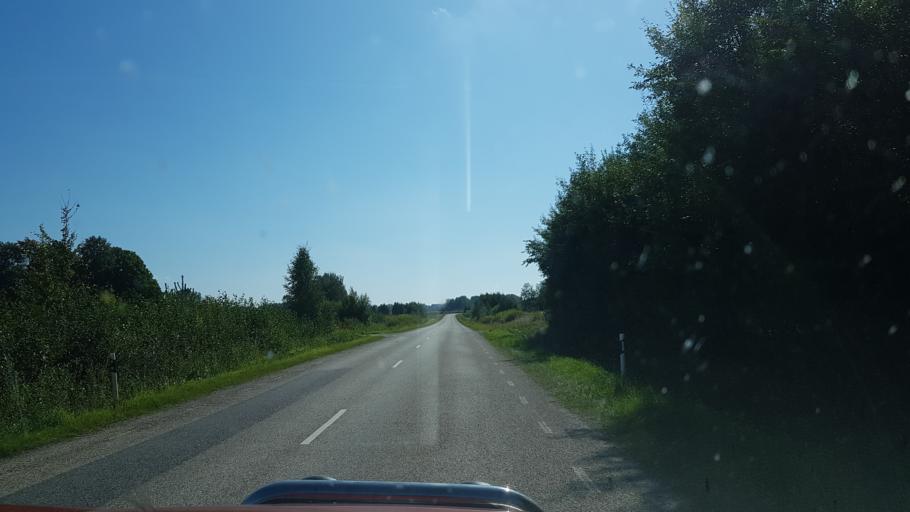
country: EE
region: Polvamaa
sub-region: Polva linn
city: Polva
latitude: 58.2392
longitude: 27.2110
